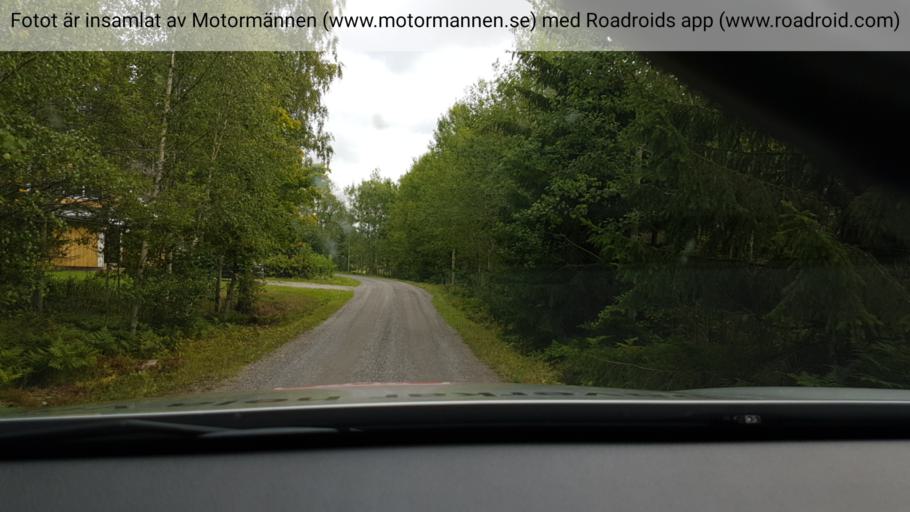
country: SE
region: Uppsala
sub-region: Heby Kommun
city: OEstervala
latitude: 60.0759
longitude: 17.2166
